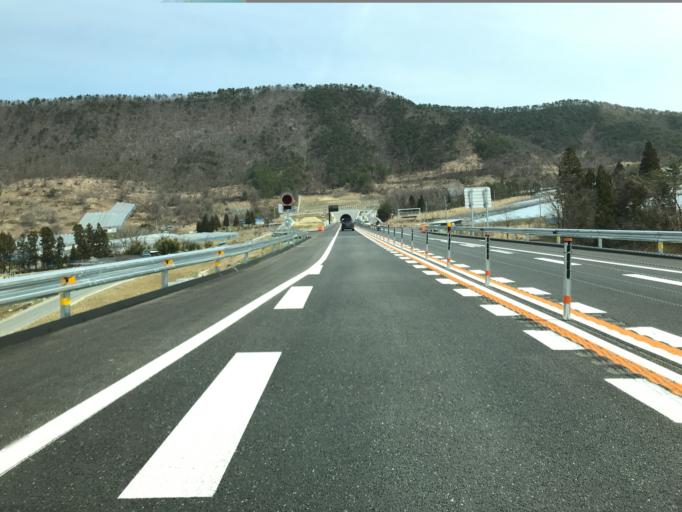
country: JP
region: Yamagata
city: Takahata
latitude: 38.0773
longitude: 140.1961
